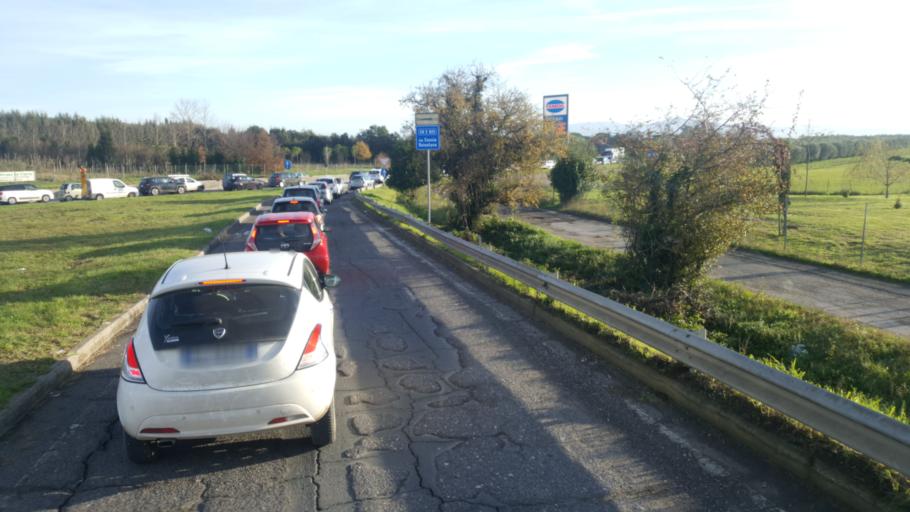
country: IT
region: Latium
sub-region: Citta metropolitana di Roma Capitale
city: Formello
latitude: 42.0447
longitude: 12.3958
